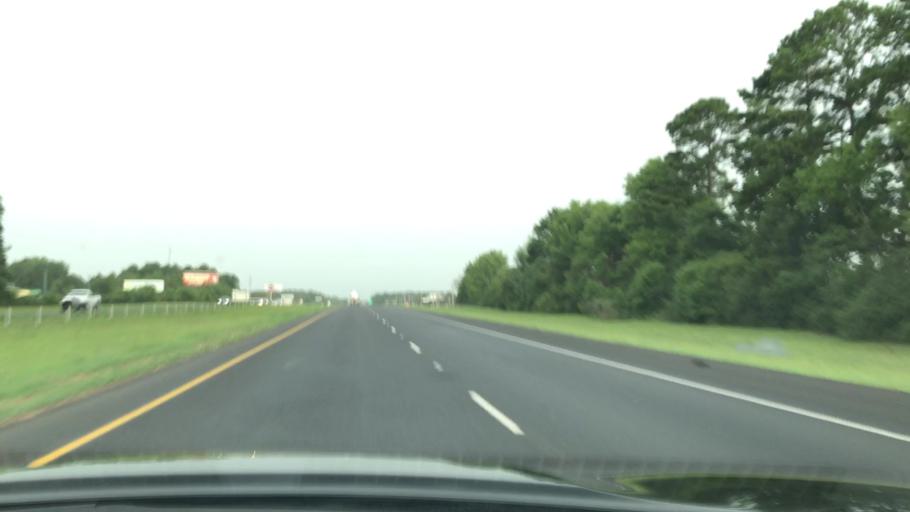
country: US
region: Louisiana
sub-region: Caddo Parish
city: Greenwood
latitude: 32.4457
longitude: -93.9177
